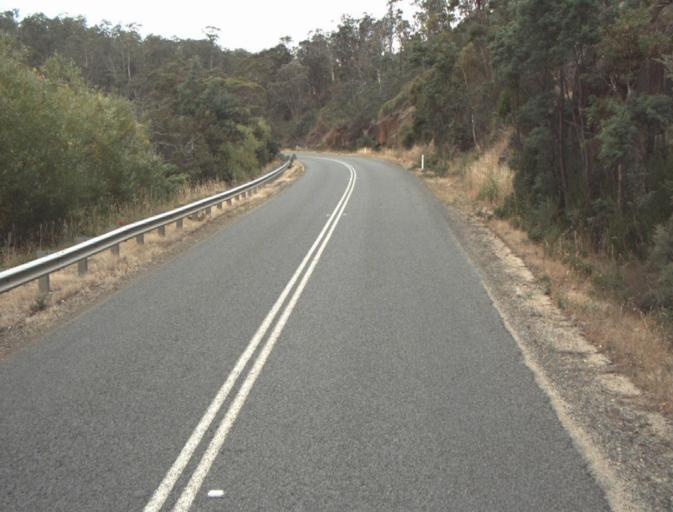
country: AU
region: Tasmania
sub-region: Northern Midlands
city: Evandale
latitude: -41.4944
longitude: 147.4242
